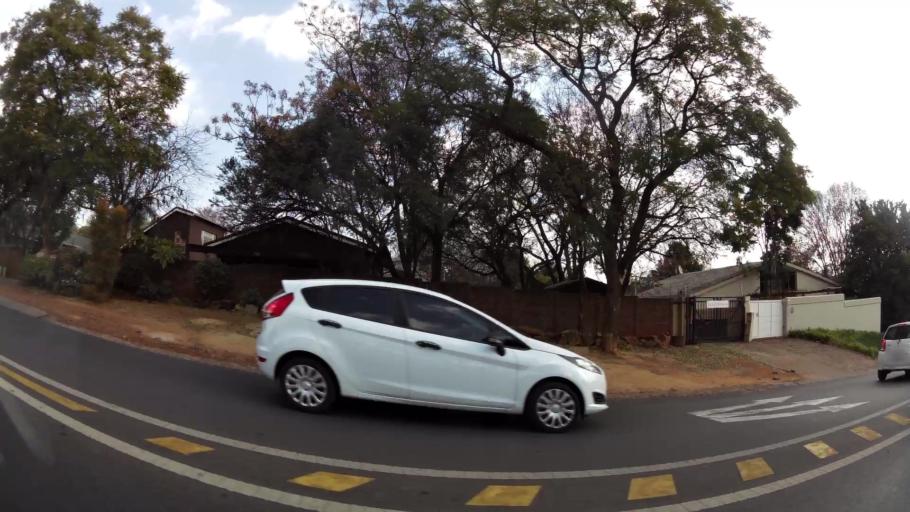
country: ZA
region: Gauteng
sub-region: City of Tshwane Metropolitan Municipality
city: Pretoria
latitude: -25.7681
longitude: 28.2793
